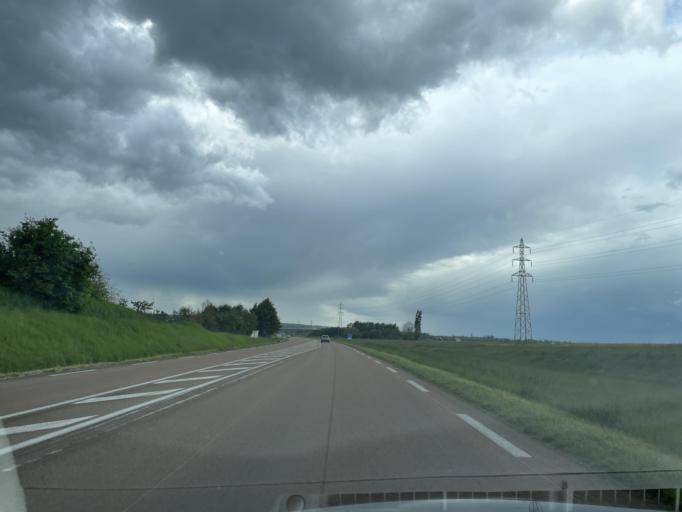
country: FR
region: Bourgogne
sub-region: Departement de l'Yonne
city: Saint-Clement
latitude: 48.2185
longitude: 3.3028
